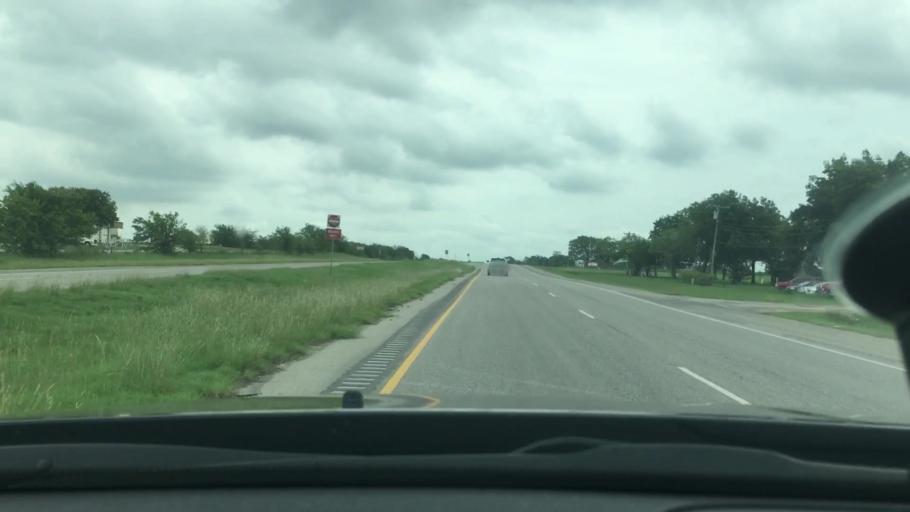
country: US
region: Oklahoma
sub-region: Carter County
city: Wilson
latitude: 34.1729
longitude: -97.4744
